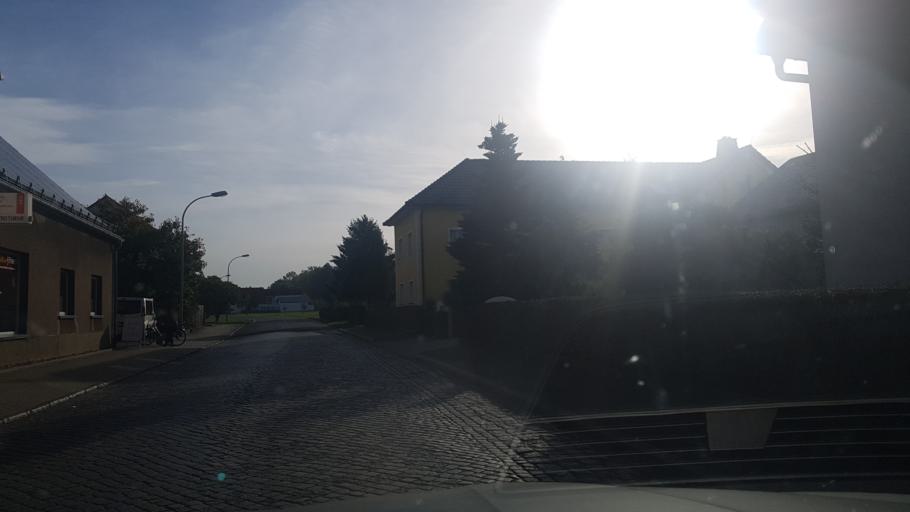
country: DE
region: Brandenburg
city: Hirschfeld
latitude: 51.3859
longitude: 13.6193
